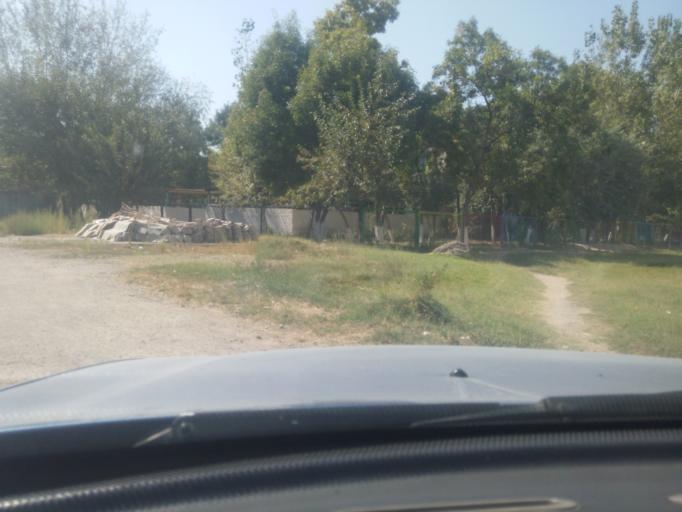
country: UZ
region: Sirdaryo
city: Guliston
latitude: 40.5164
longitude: 68.7776
